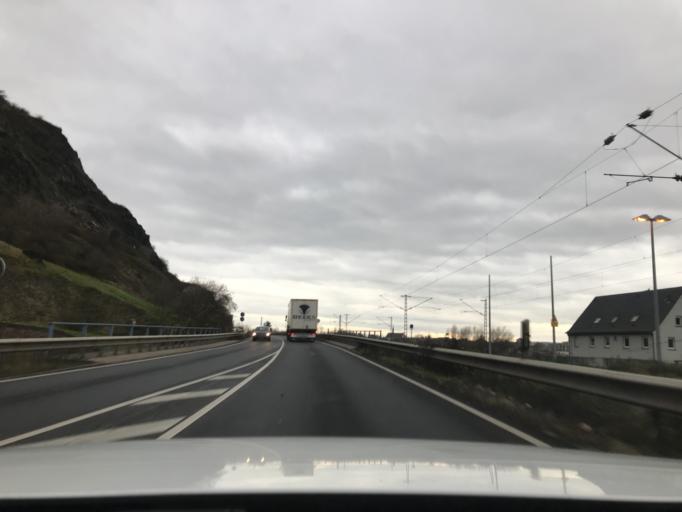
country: DE
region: Rheinland-Pfalz
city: Leutesdorf
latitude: 50.4470
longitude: 7.3934
